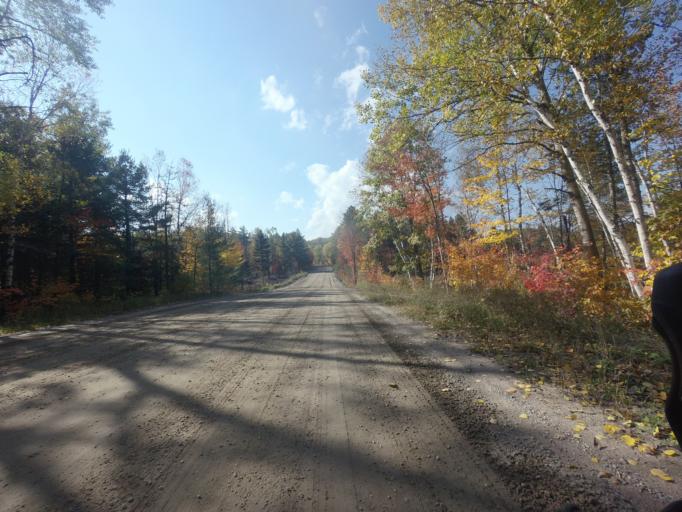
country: CA
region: Ontario
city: Petawawa
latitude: 45.8214
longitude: -77.4418
